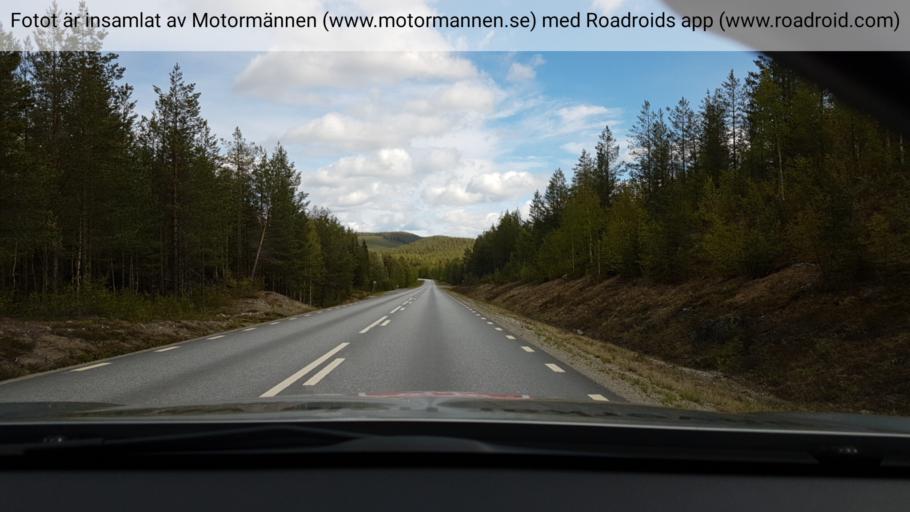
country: SE
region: Vaesterbotten
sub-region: Asele Kommun
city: Insjon
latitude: 64.1987
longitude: 17.6619
